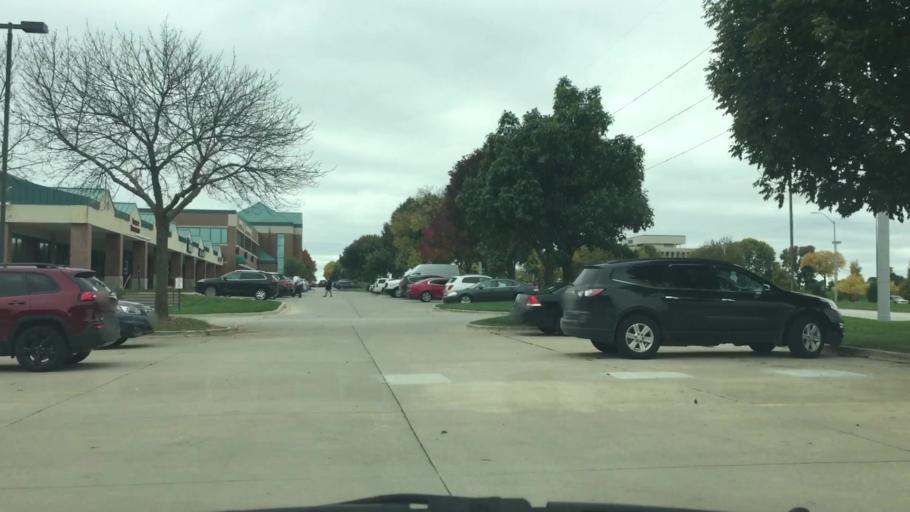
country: US
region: Iowa
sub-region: Polk County
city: Clive
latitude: 41.5976
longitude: -93.7708
